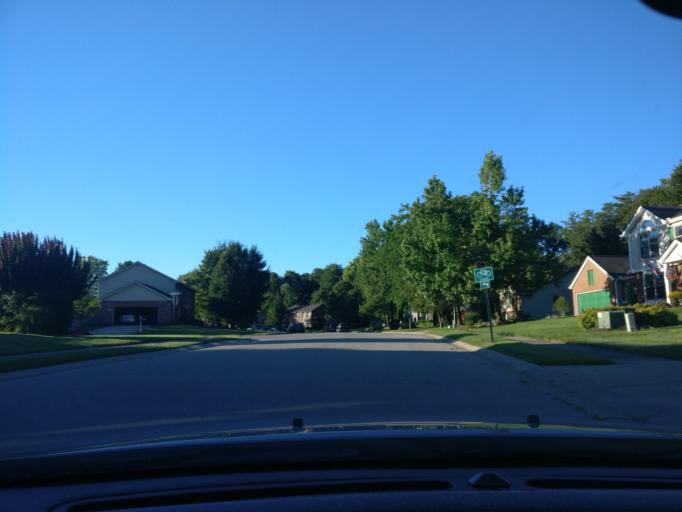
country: US
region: Ohio
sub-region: Warren County
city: Springboro
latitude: 39.5710
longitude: -84.2423
